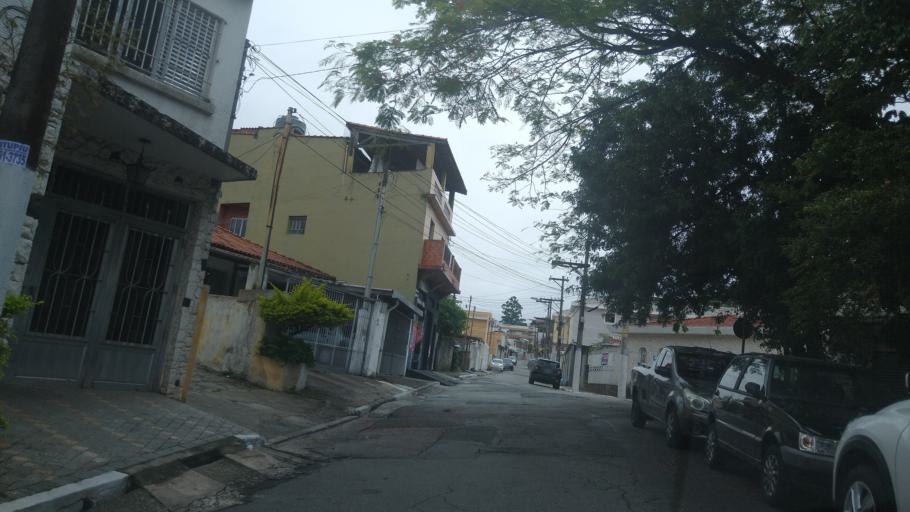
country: BR
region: Sao Paulo
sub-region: Sao Paulo
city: Sao Paulo
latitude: -23.4945
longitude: -46.6073
